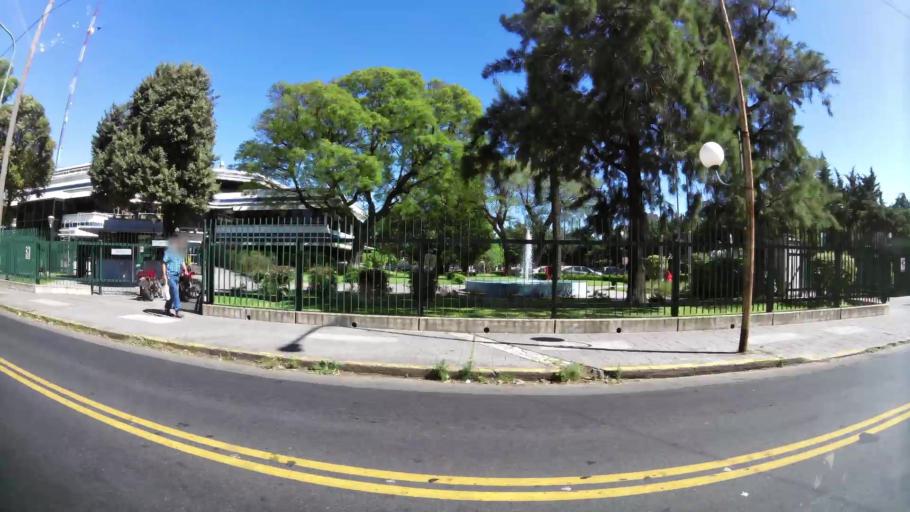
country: AR
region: Buenos Aires
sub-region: Partido de Vicente Lopez
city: Olivos
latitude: -34.5244
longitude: -58.5123
